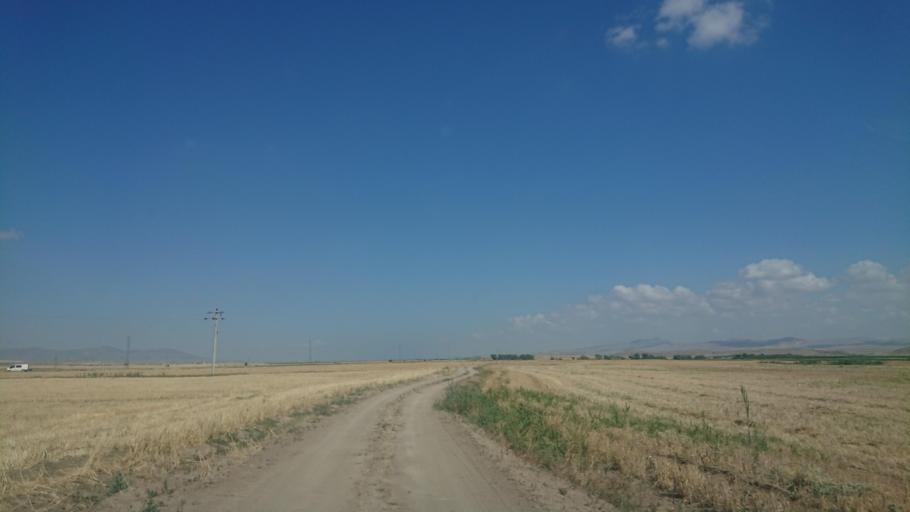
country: TR
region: Aksaray
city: Sariyahsi
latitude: 38.9856
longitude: 33.9043
